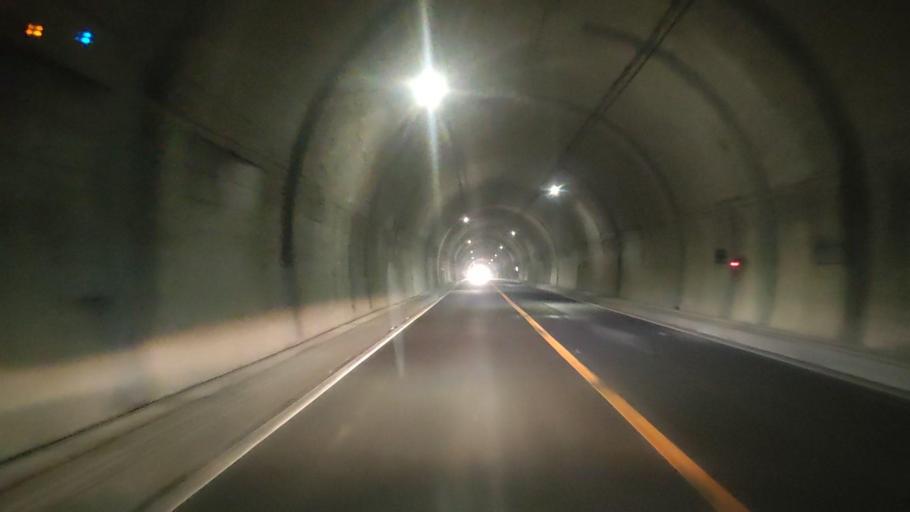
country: JP
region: Oita
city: Saiki
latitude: 32.8824
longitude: 131.9469
